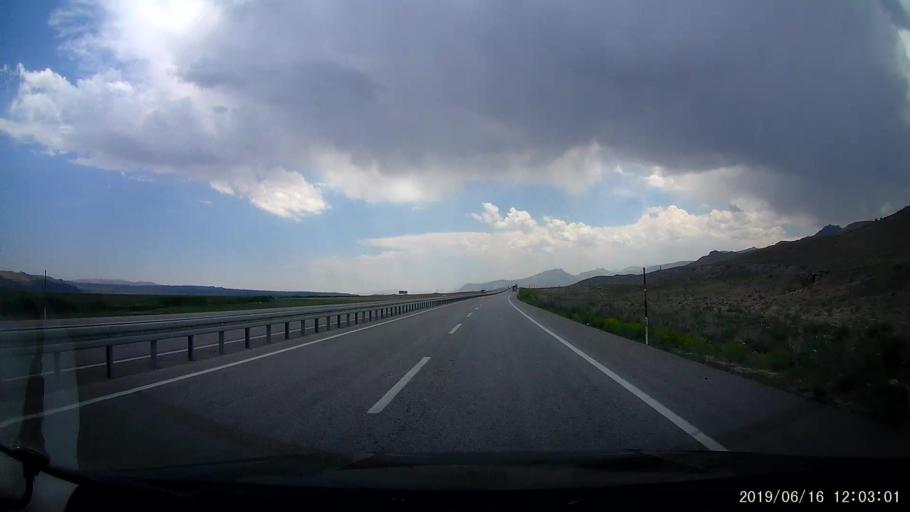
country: TR
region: Agri
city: Dogubayazit
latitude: 39.5436
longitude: 44.2241
